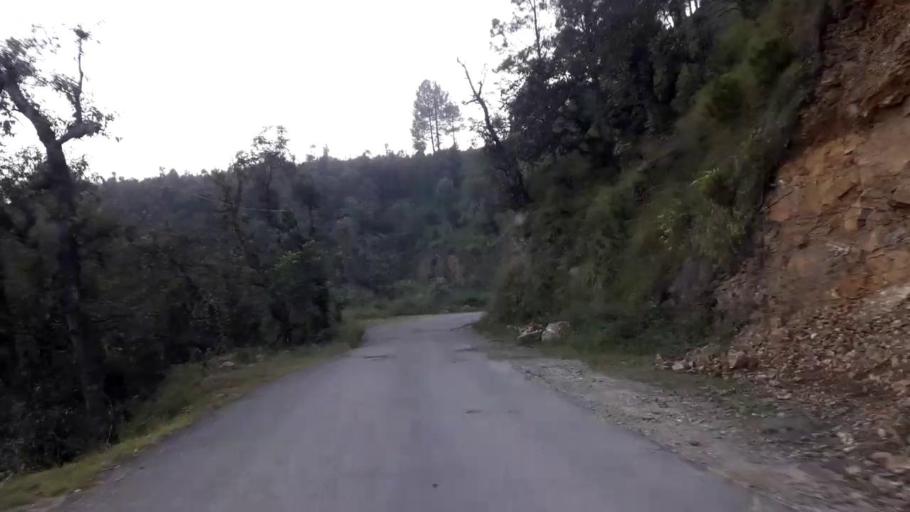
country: IN
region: Himachal Pradesh
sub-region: Shimla
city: Shimla
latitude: 31.0543
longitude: 77.1551
